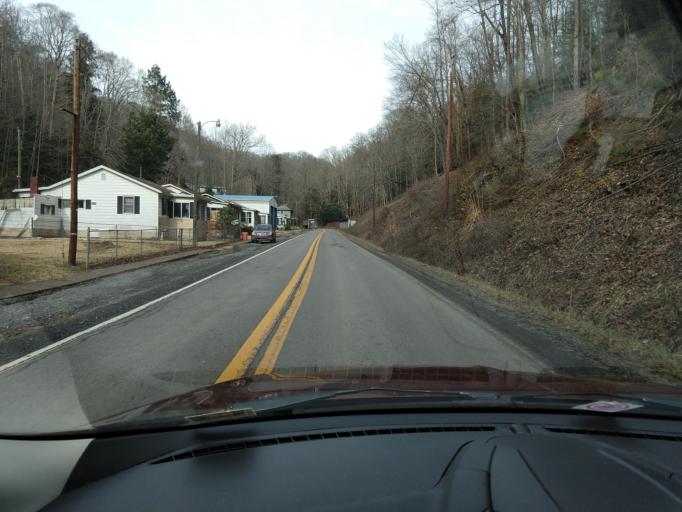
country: US
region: West Virginia
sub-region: McDowell County
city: Welch
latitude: 37.3379
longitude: -81.6723
